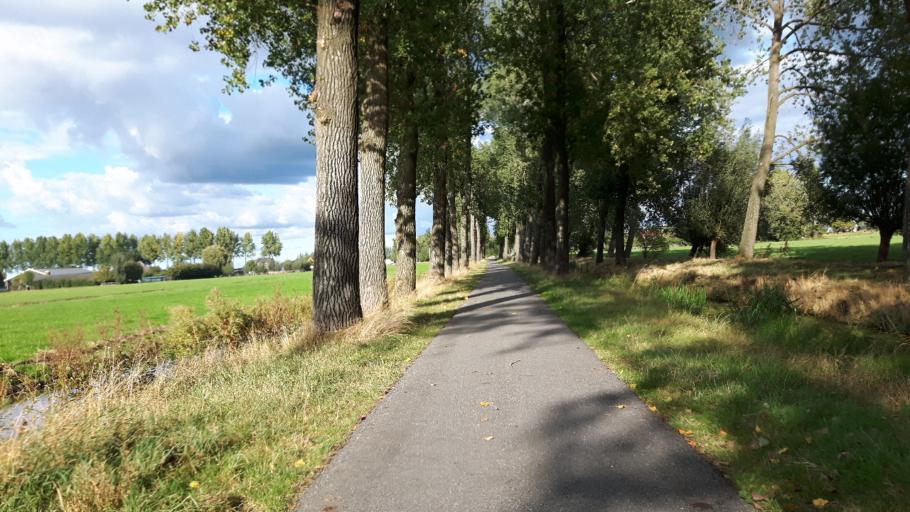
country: NL
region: South Holland
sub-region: Gemeente Leerdam
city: Leerdam
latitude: 51.9373
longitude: 5.0961
